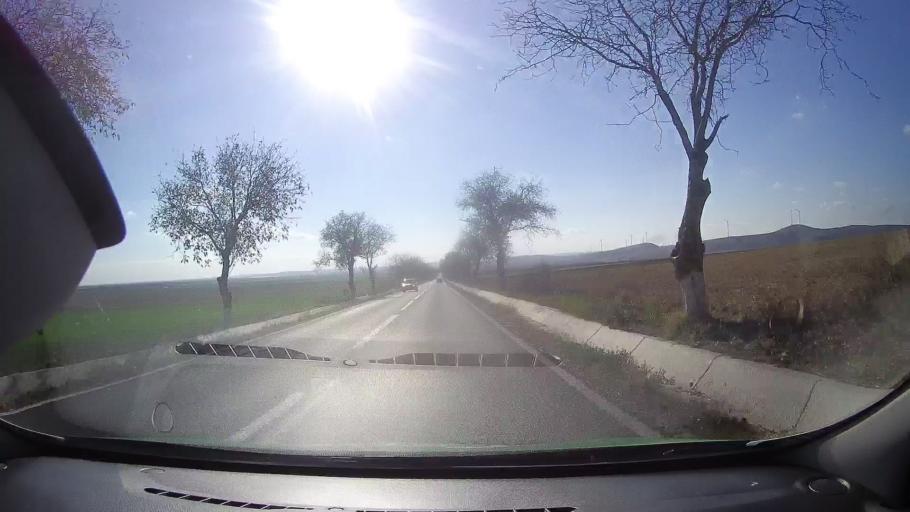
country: RO
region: Tulcea
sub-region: Comuna Ceamurlia de Jos
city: Ceamurlia de Jos
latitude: 44.8046
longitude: 28.6908
